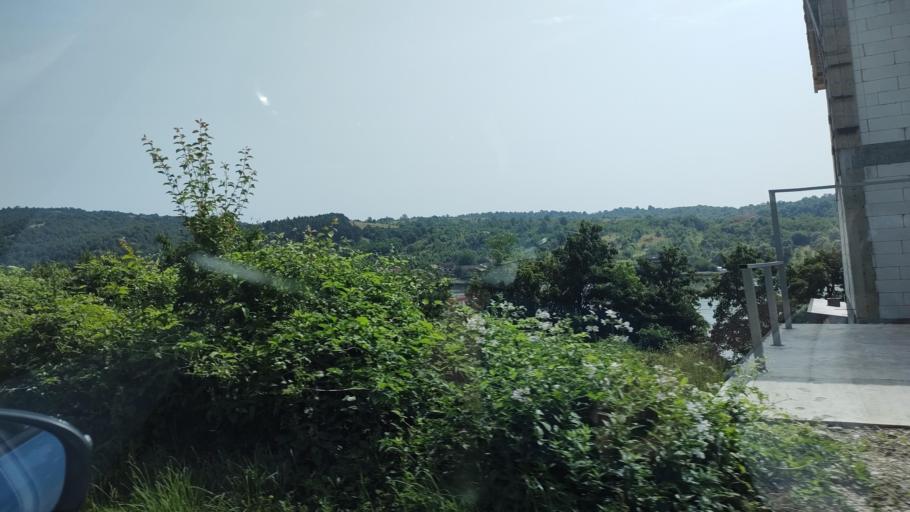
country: RO
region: Mehedinti
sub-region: Comuna Eselnita
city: Eselnita
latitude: 44.6885
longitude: 22.3633
